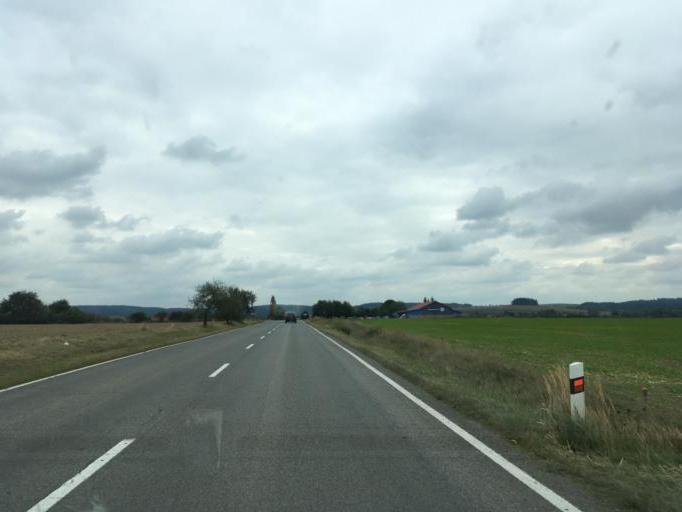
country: CZ
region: Vysocina
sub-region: Okres Pelhrimov
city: Zeliv
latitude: 49.5196
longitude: 15.1736
